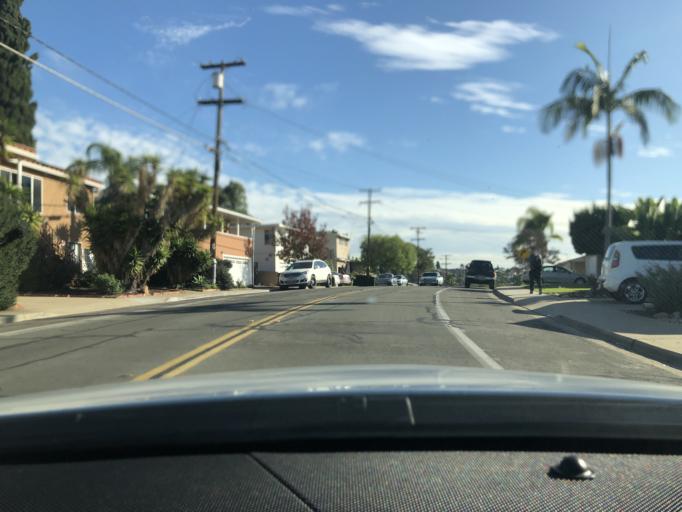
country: US
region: California
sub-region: San Diego County
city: Lemon Grove
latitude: 32.7539
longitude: -117.0723
